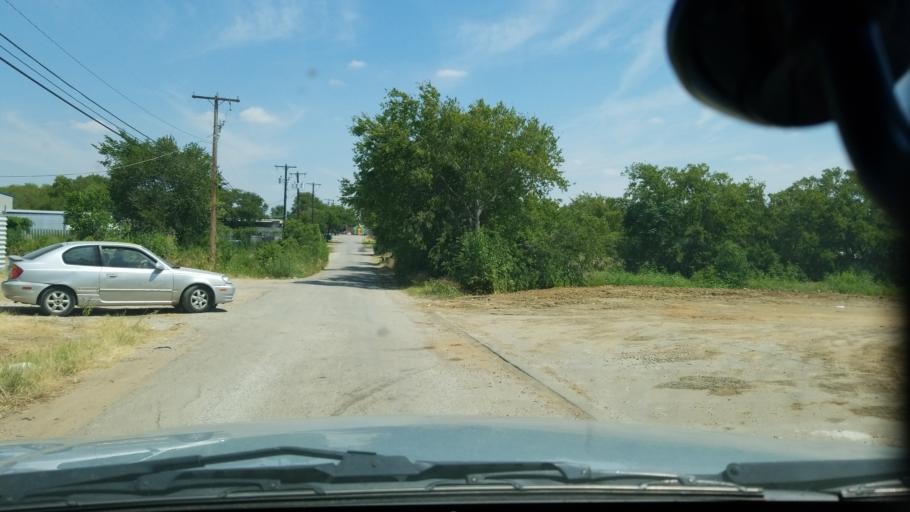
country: US
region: Texas
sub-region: Dallas County
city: Grand Prairie
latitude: 32.7440
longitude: -96.9568
